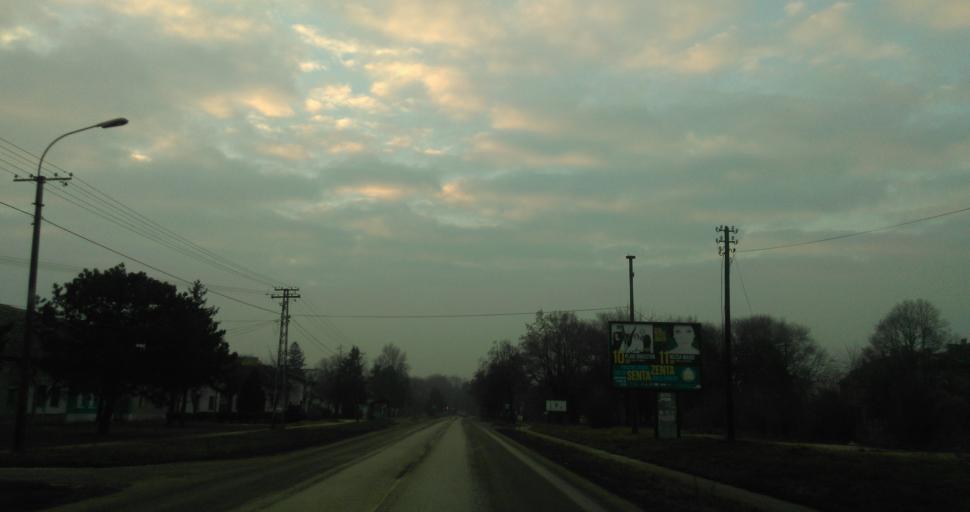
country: RS
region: Autonomna Pokrajina Vojvodina
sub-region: Juznobacki Okrug
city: Becej
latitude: 45.6253
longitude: 20.0357
